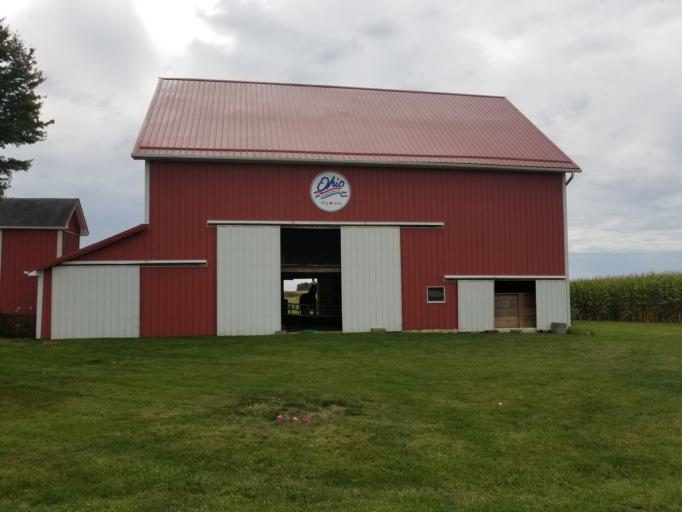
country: US
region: Ohio
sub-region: Knox County
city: Centerburg
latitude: 40.2595
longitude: -82.7184
